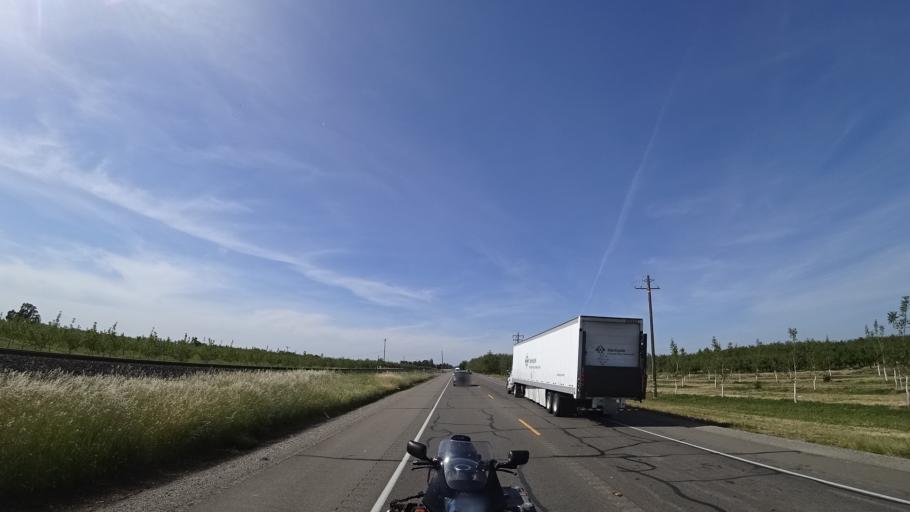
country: US
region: California
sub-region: Tehama County
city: Los Molinos
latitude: 40.0021
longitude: -122.0904
